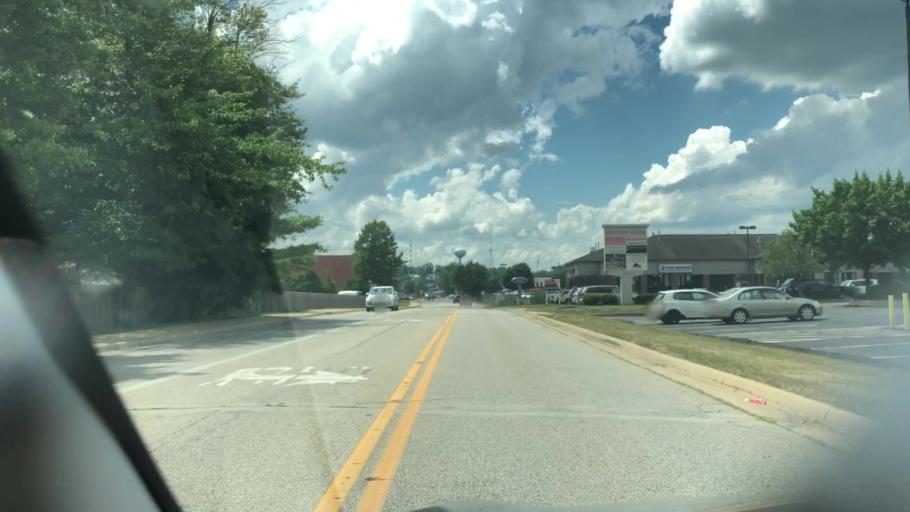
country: US
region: Ohio
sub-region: Summit County
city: Montrose-Ghent
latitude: 41.1334
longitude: -81.6397
